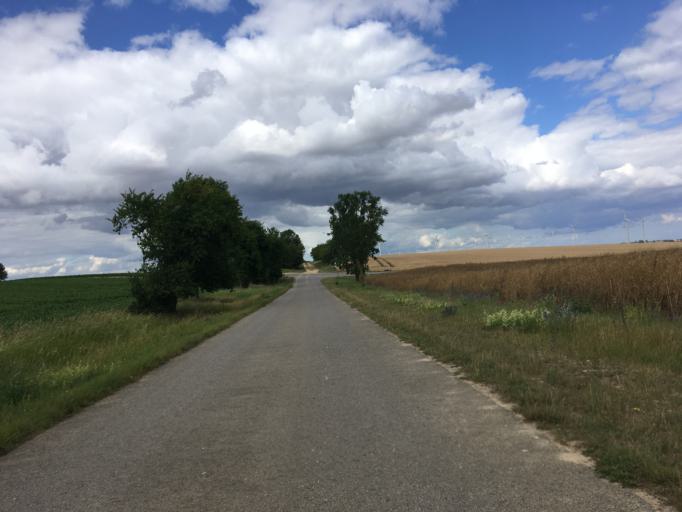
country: DE
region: Brandenburg
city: Gramzow
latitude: 53.2615
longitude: 14.0174
